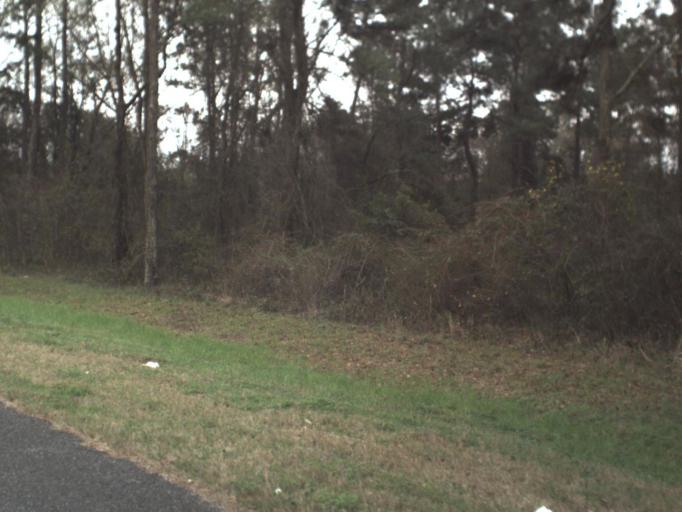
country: US
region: Florida
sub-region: Leon County
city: Tallahassee
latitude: 30.4193
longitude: -84.1568
